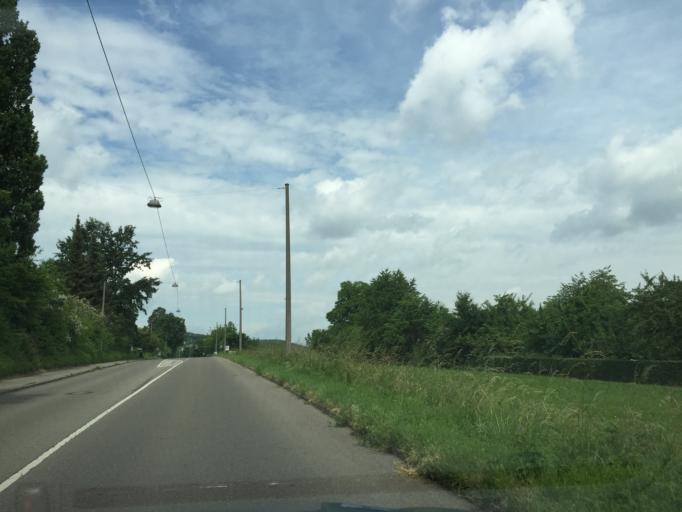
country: DE
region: Baden-Wuerttemberg
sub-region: Tuebingen Region
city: Ulm
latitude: 48.3967
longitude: 9.9481
